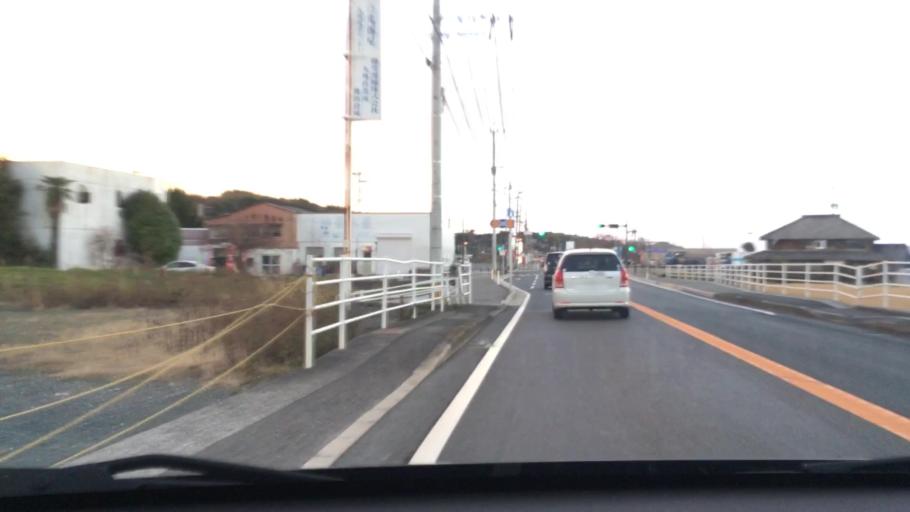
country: JP
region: Fukuoka
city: Shiida
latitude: 33.6328
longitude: 131.0799
